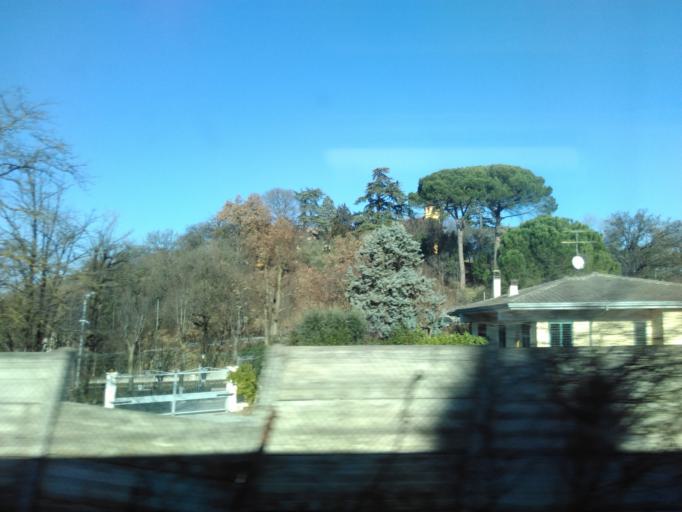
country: IT
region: Lombardy
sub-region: Provincia di Brescia
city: Desenzano del Garda
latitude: 45.4683
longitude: 10.5208
